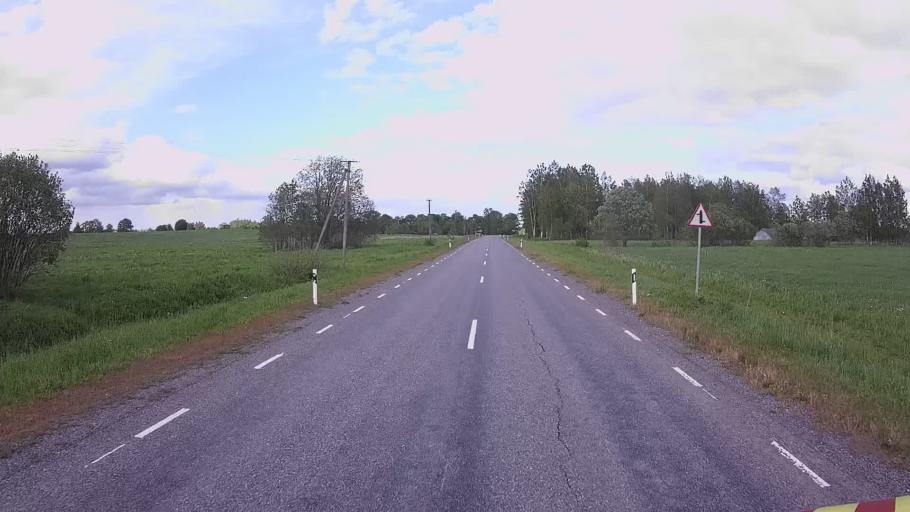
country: EE
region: Jogevamaa
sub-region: Mustvee linn
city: Mustvee
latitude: 59.0154
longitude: 26.9432
